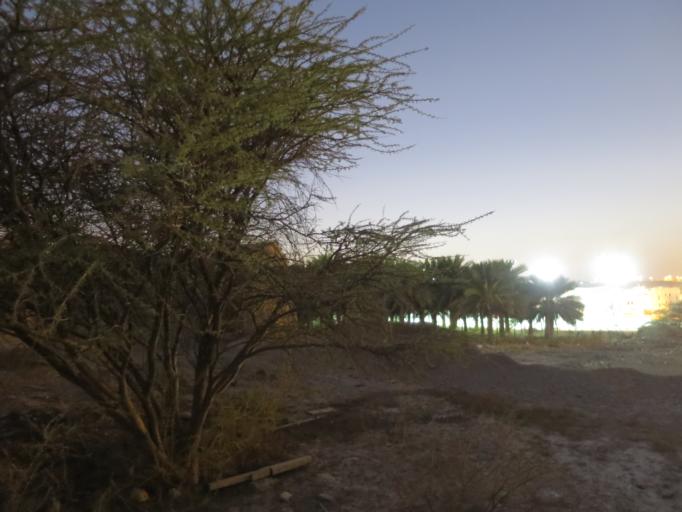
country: OM
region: Muhafazat Masqat
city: Bawshar
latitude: 23.5515
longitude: 58.4075
